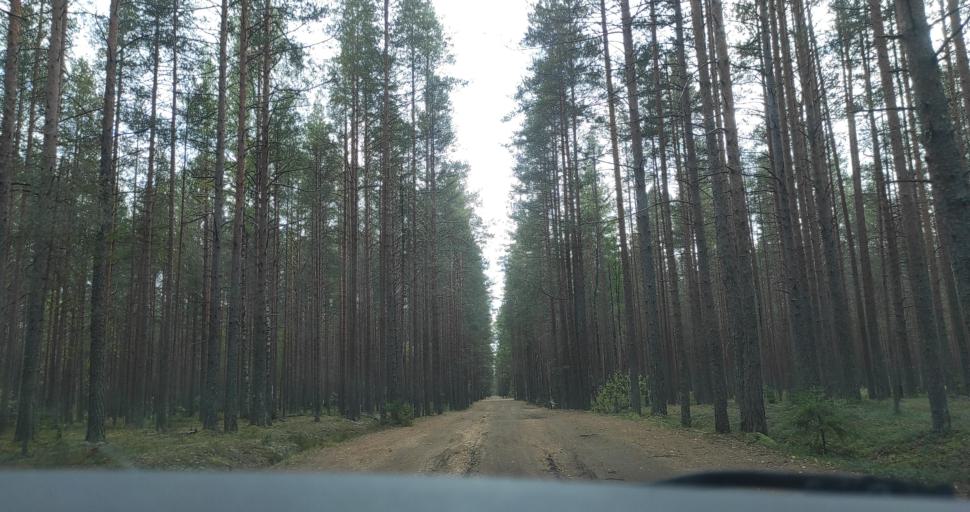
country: RU
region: Leningrad
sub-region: Vsevolzhskij Rajon
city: Vaskelovo
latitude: 60.4105
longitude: 30.3287
